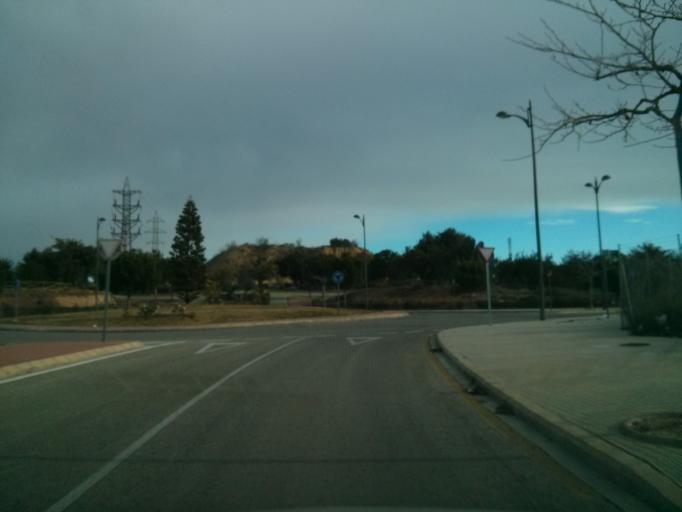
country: ES
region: Valencia
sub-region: Provincia de Valencia
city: Manises
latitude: 39.5241
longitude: -0.4605
